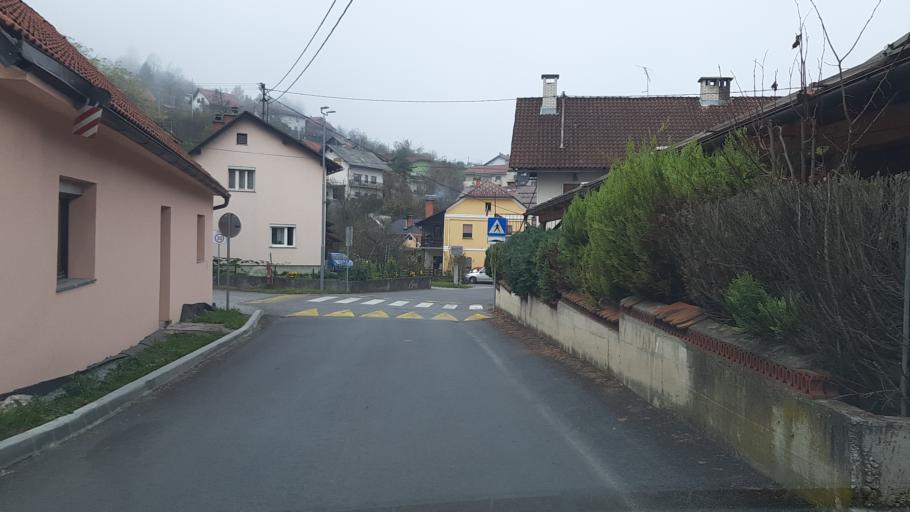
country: SI
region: Borovnica
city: Borovnica
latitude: 45.9162
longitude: 14.3652
